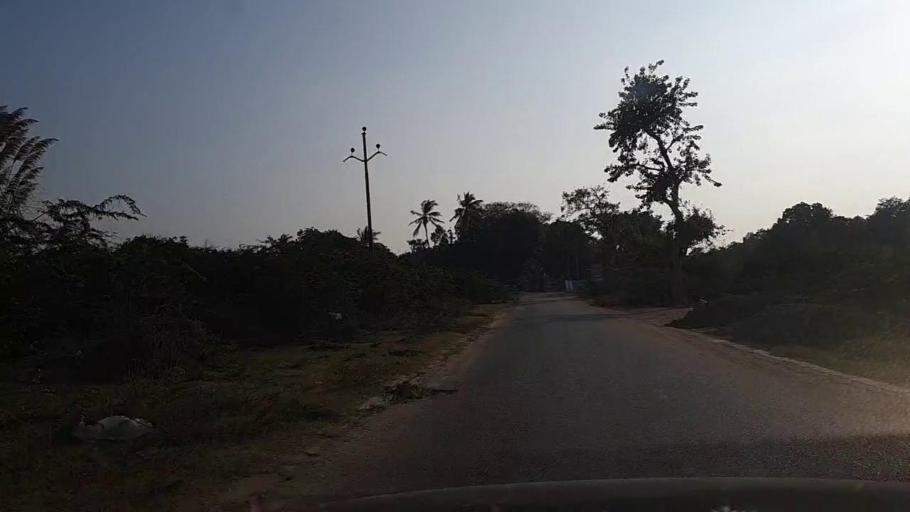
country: PK
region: Sindh
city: Gharo
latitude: 24.7783
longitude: 67.5101
